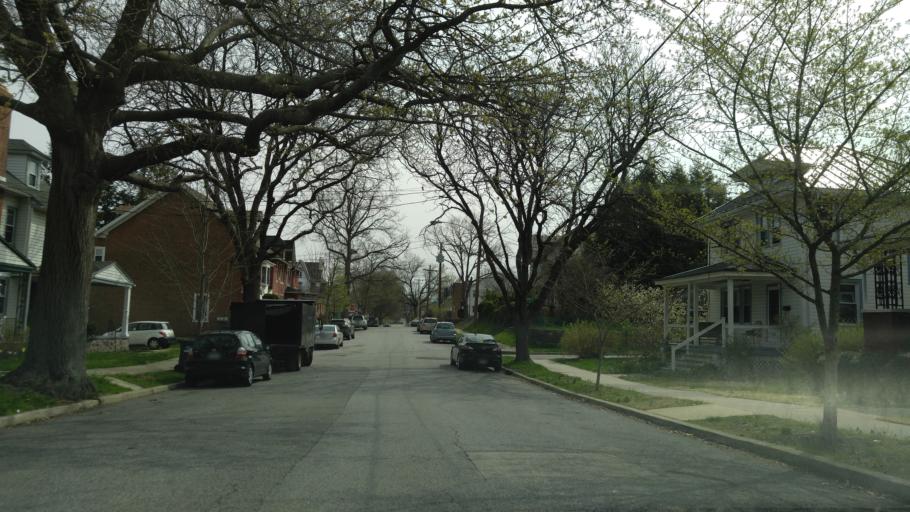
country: US
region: Pennsylvania
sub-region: Chester County
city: Phoenixville
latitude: 40.1293
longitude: -75.5161
